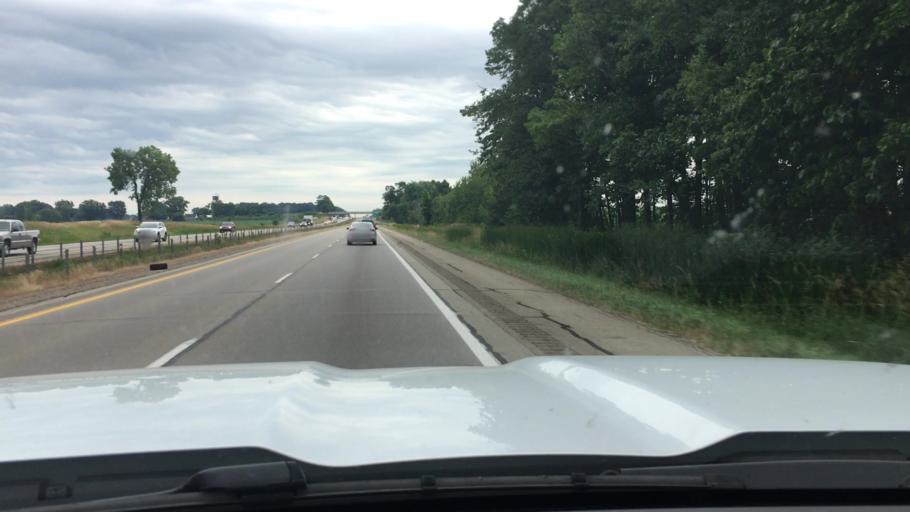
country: US
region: Michigan
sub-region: Allegan County
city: Wayland
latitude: 42.7472
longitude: -85.6736
